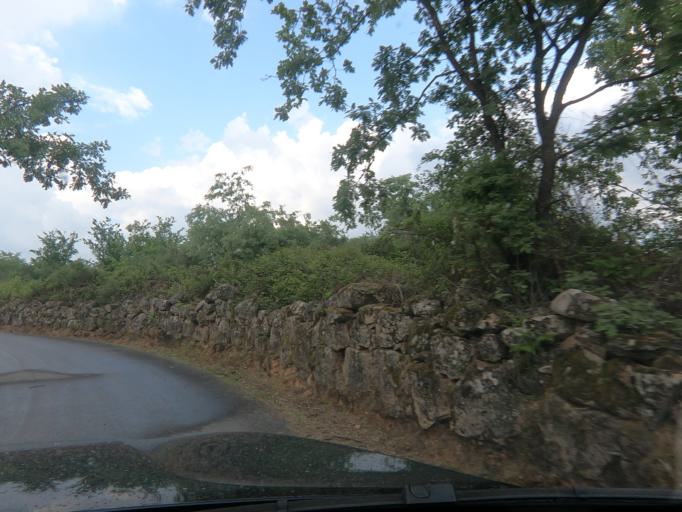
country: PT
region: Vila Real
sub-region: Vila Real
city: Vila Real
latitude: 41.3074
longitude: -7.7120
